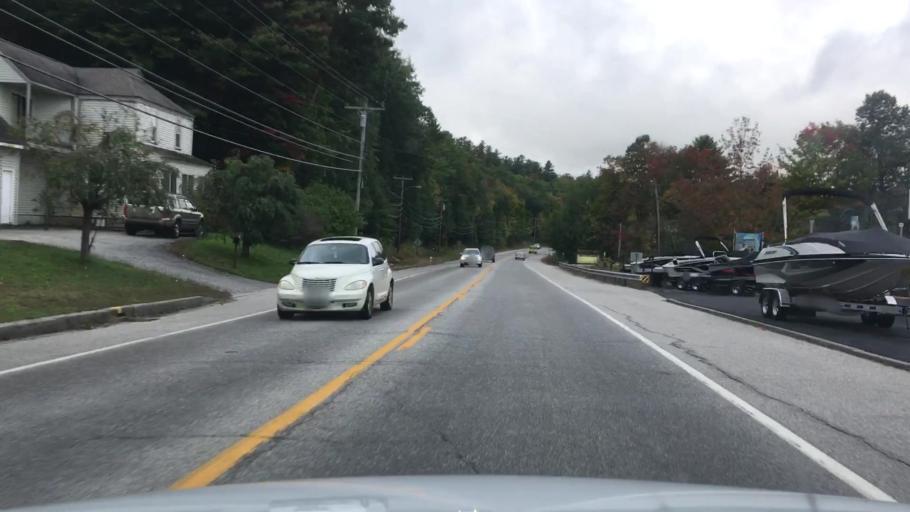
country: US
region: Maine
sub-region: Oxford County
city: Norway
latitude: 44.2135
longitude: -70.5556
